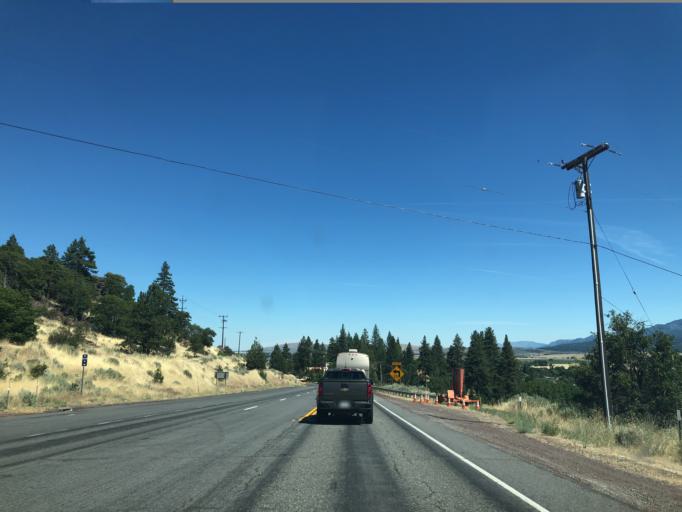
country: US
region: California
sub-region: Lassen County
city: Susanville
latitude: 40.4184
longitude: -120.6704
